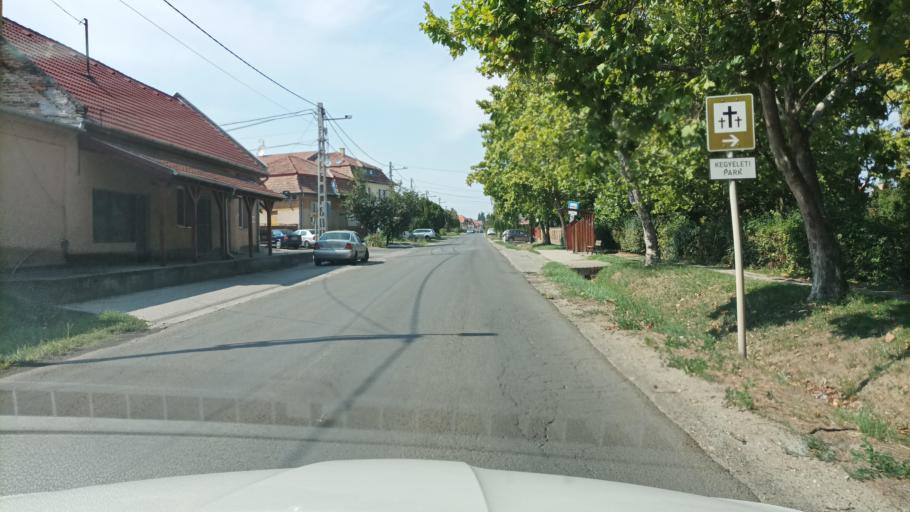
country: HU
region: Pest
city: Galgaheviz
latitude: 47.6223
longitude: 19.5482
